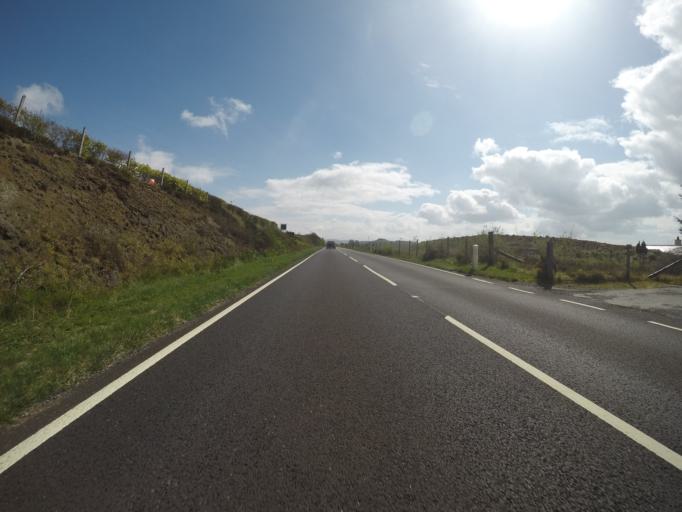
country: GB
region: Scotland
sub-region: Highland
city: Portree
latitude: 57.4975
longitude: -6.3228
